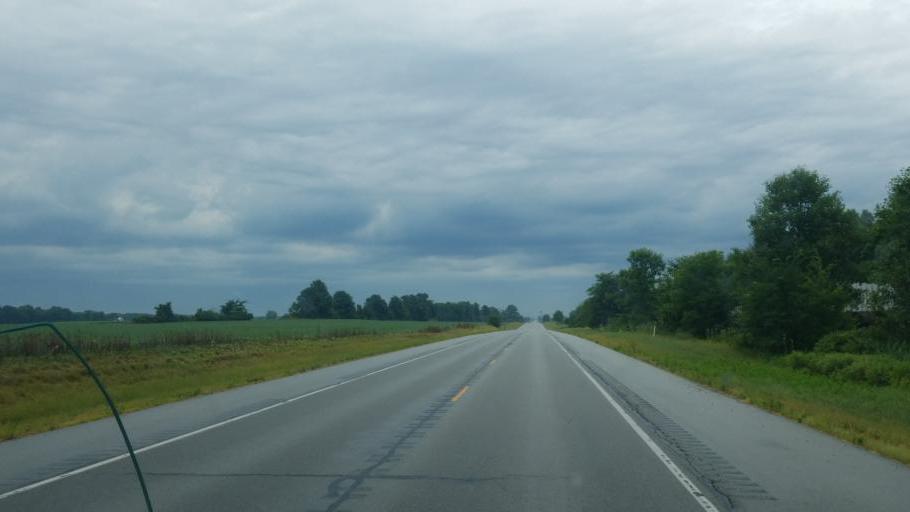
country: US
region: Indiana
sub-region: DeKalb County
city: Butler
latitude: 41.4356
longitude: -84.8226
